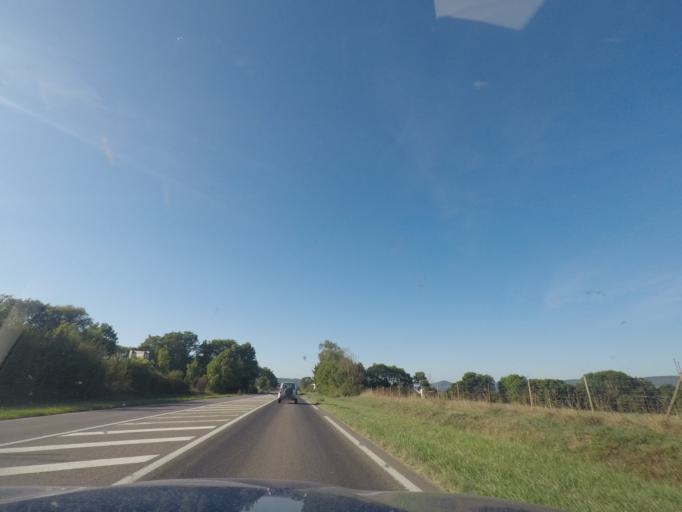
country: FR
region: Lorraine
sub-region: Departement de la Moselle
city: Hettange-Grande
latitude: 49.4221
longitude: 6.1617
